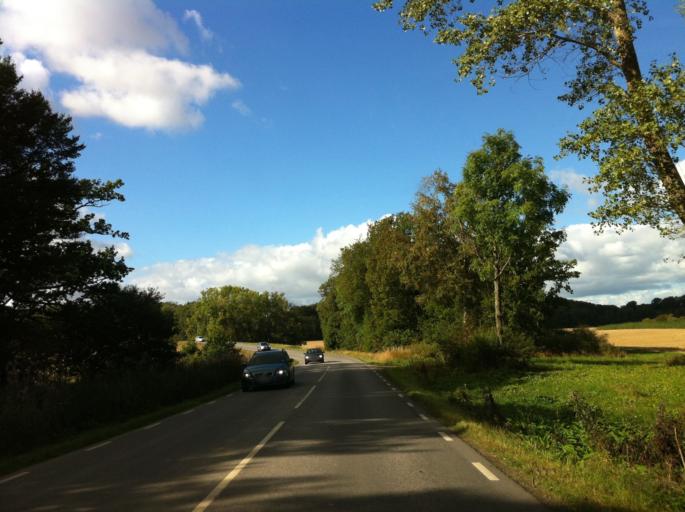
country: SE
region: Skane
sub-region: Tomelilla Kommun
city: Tomelilla
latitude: 55.6502
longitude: 13.9487
